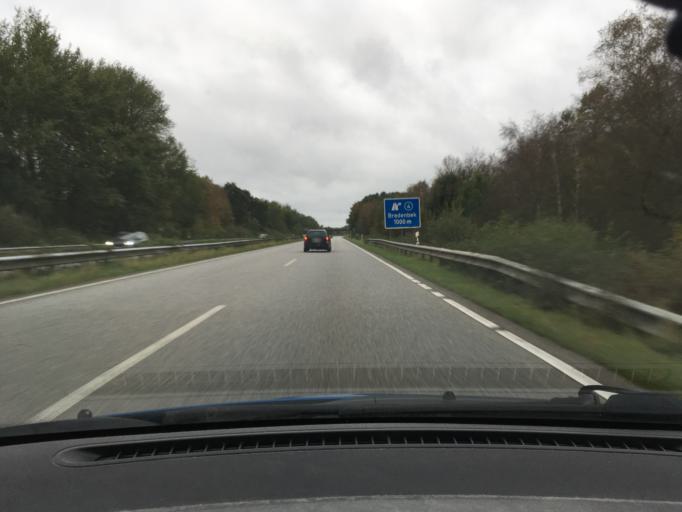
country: DE
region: Schleswig-Holstein
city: Bredenbek
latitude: 54.3148
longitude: 9.8773
